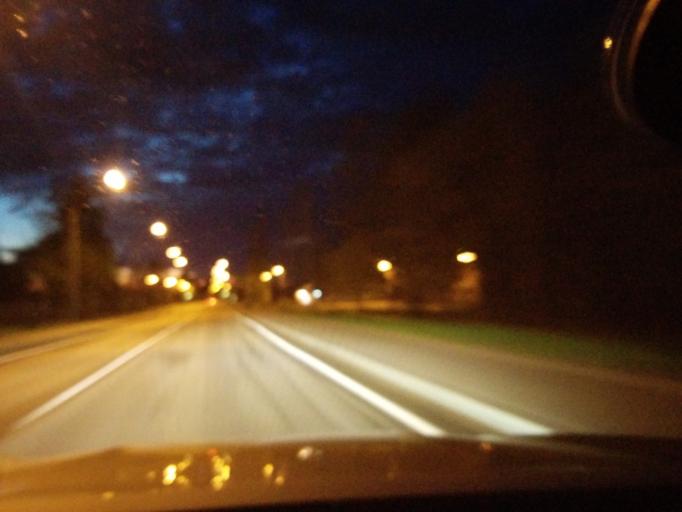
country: RU
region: Leningrad
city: Verkhniye Osel'ki
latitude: 60.2469
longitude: 30.4453
